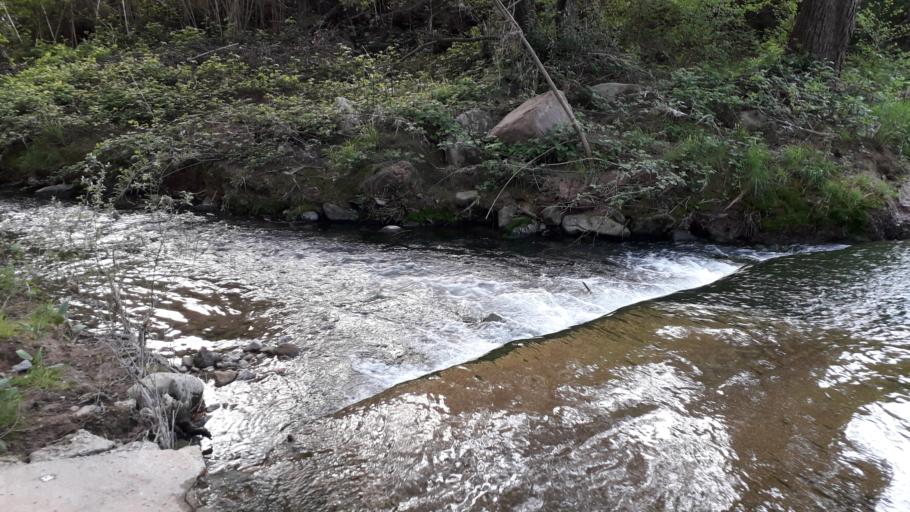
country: ES
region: Catalonia
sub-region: Provincia de Barcelona
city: Jorba
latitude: 41.5948
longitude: 1.5482
